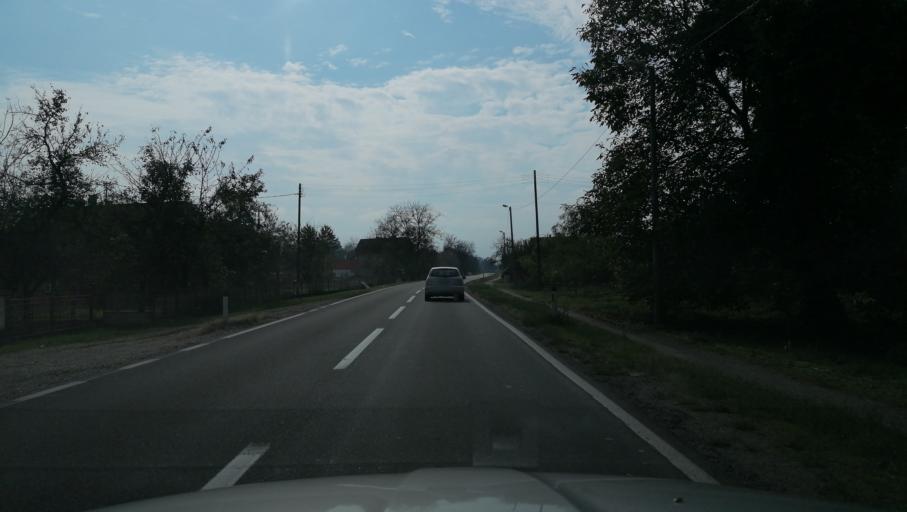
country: BA
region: Republika Srpska
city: Balatun
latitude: 44.8664
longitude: 19.3293
